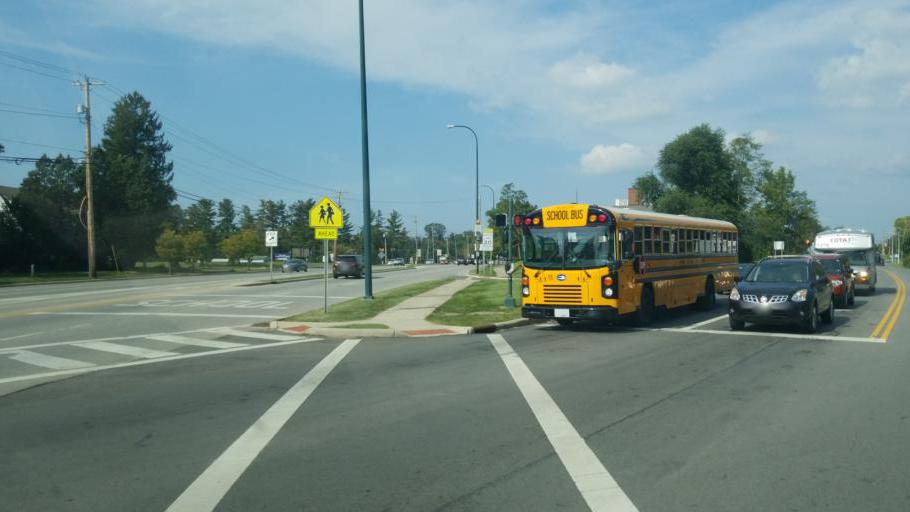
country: US
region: Ohio
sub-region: Franklin County
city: Gahanna
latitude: 40.0385
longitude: -82.8648
